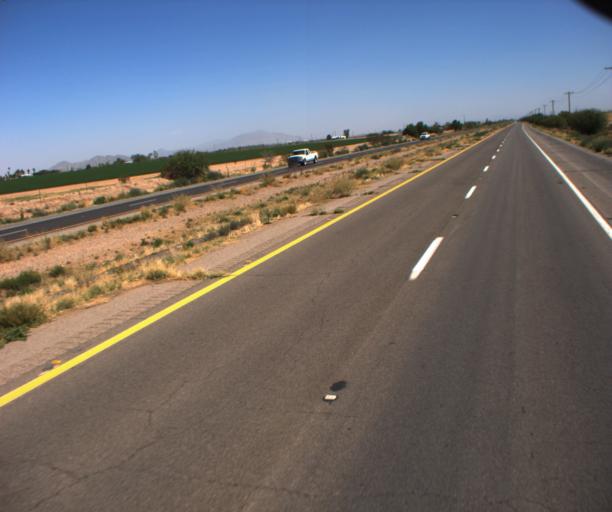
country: US
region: Arizona
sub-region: Pinal County
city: Maricopa
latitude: 32.8950
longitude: -112.0493
